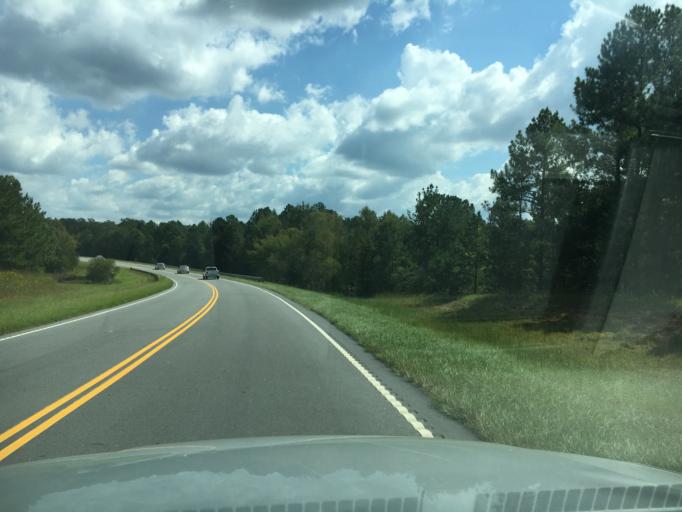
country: US
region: South Carolina
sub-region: Greenwood County
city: Greenwood
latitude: 34.1383
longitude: -82.1424
